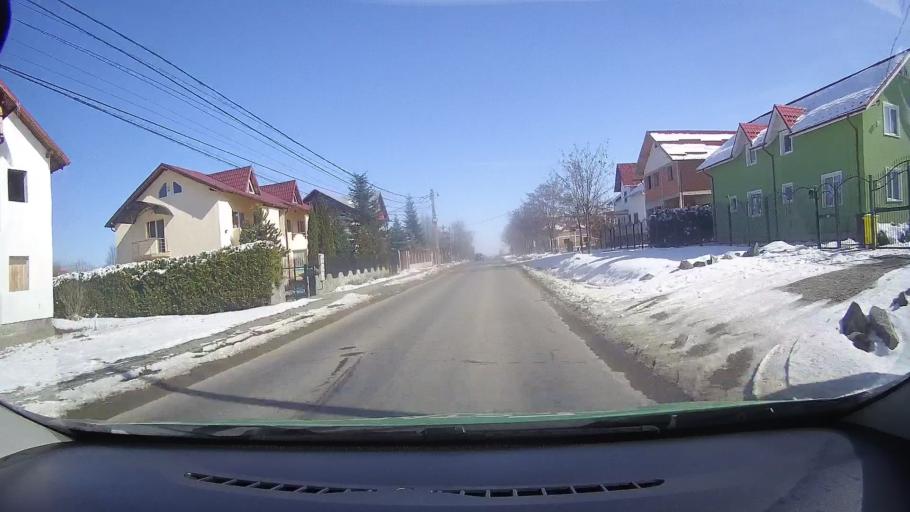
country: RO
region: Brasov
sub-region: Oras Victoria
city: Victoria
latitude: 45.7271
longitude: 24.7062
